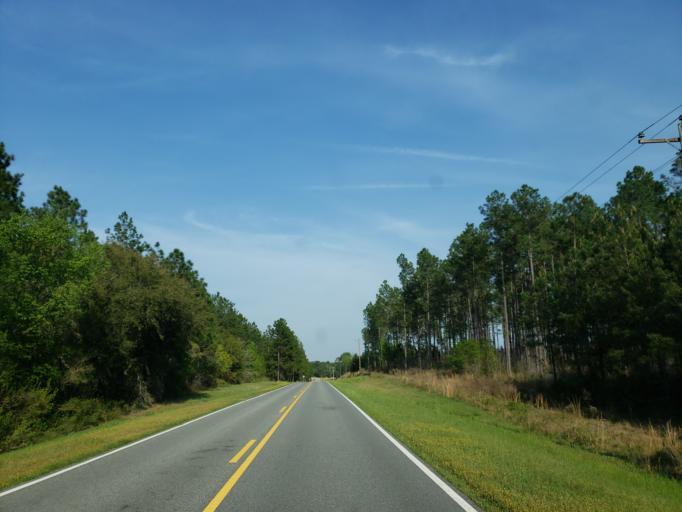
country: US
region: Georgia
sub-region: Tift County
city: Tifton
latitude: 31.5737
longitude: -83.5068
